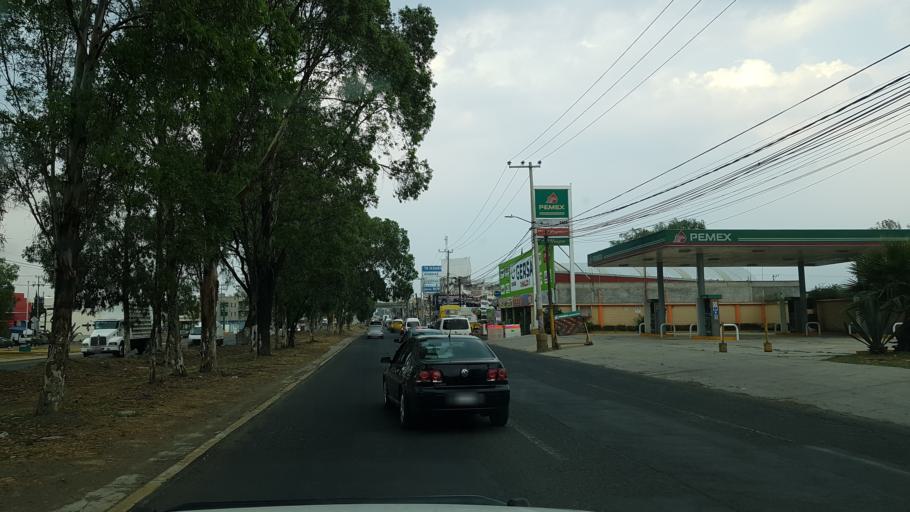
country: MX
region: Mexico
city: Chalco de Diaz Covarrubias
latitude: 19.2765
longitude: -98.8829
